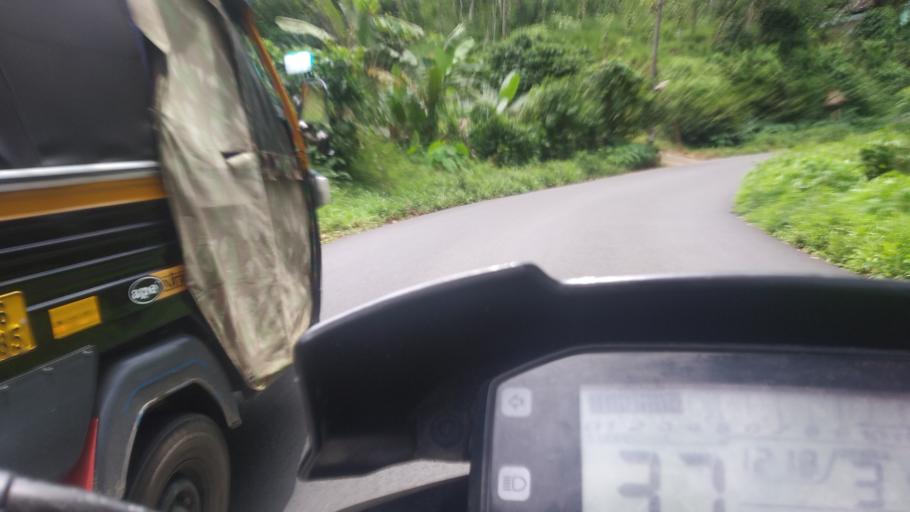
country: IN
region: Kerala
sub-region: Idukki
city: Munnar
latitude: 10.0170
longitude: 77.0086
